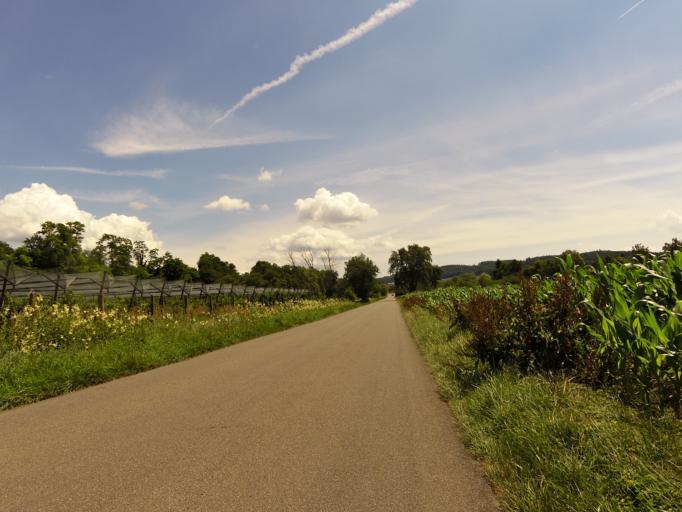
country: DE
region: Baden-Wuerttemberg
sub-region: Tuebingen Region
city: Uhldingen-Muhlhofen
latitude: 47.7389
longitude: 9.2325
